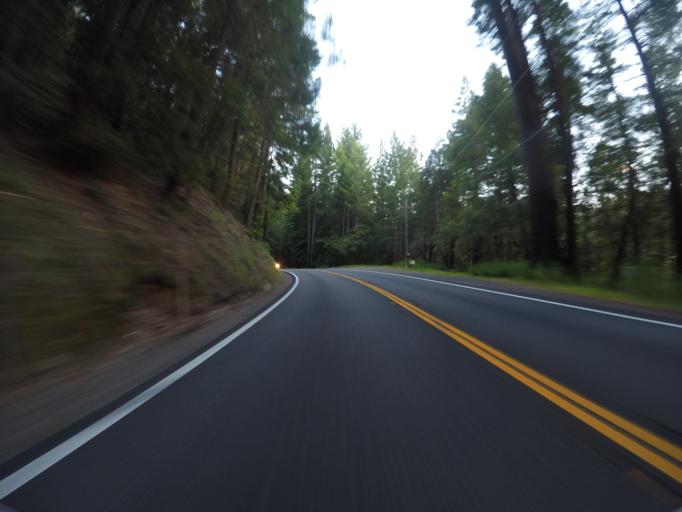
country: US
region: California
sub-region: Humboldt County
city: Redway
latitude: 39.9111
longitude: -123.7578
